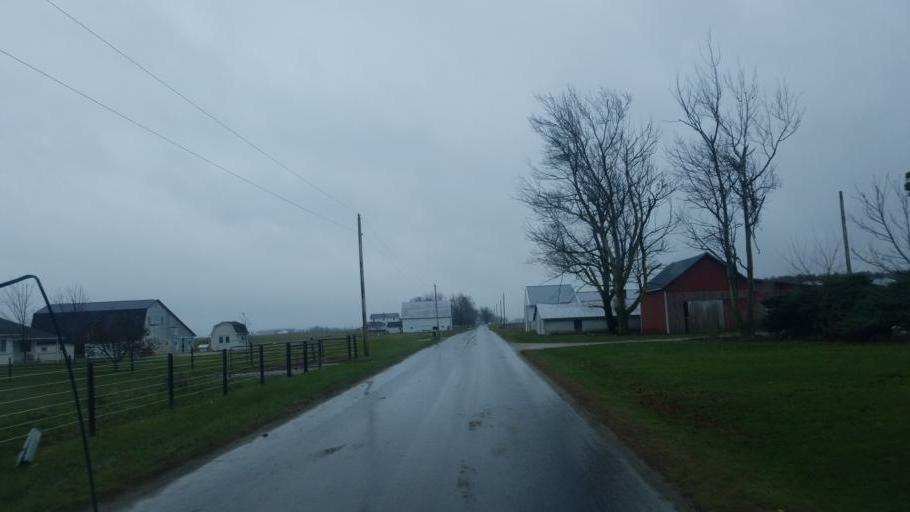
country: US
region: Indiana
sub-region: Adams County
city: Berne
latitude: 40.6416
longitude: -84.8783
